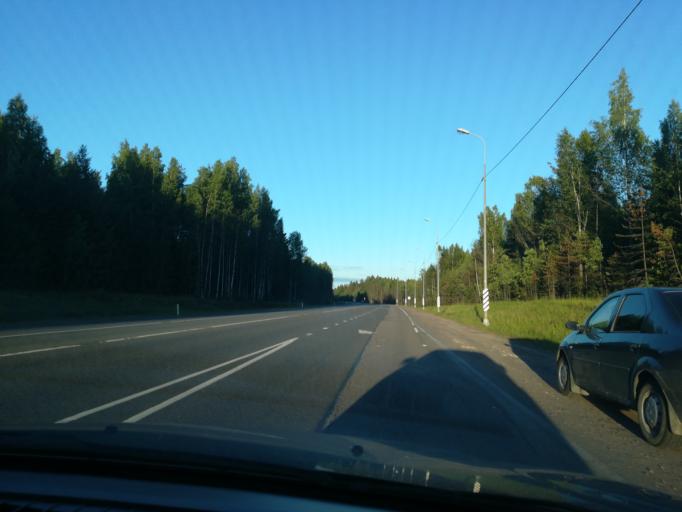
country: RU
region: Leningrad
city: Veshchevo
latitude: 60.6015
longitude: 29.1036
